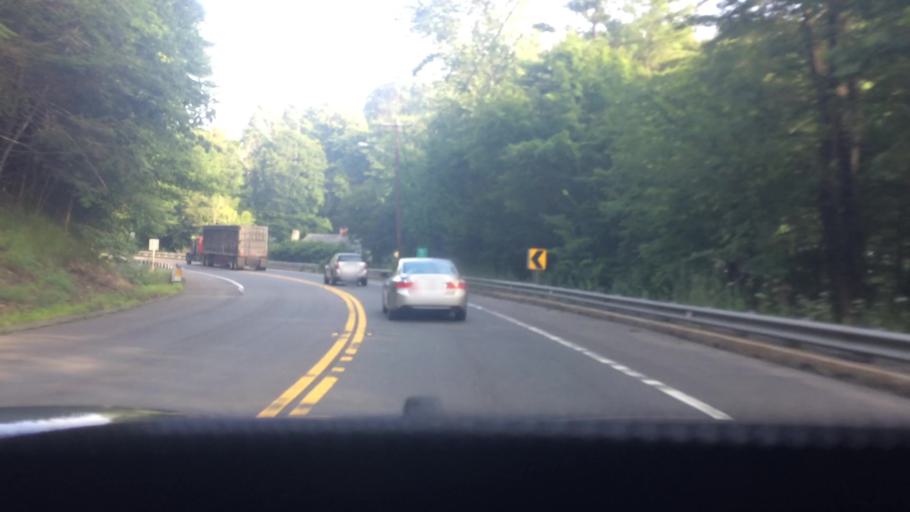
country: US
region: Massachusetts
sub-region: Franklin County
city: Turners Falls
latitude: 42.6166
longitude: -72.5524
